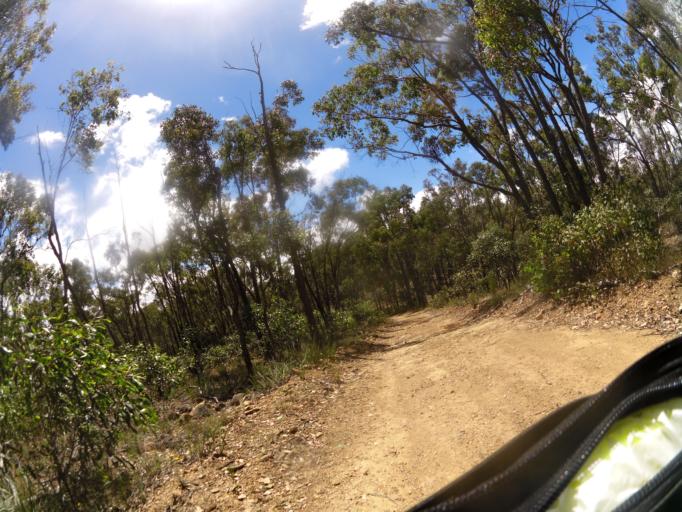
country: AU
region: Victoria
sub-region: Mount Alexander
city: Castlemaine
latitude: -37.0659
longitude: 144.2652
